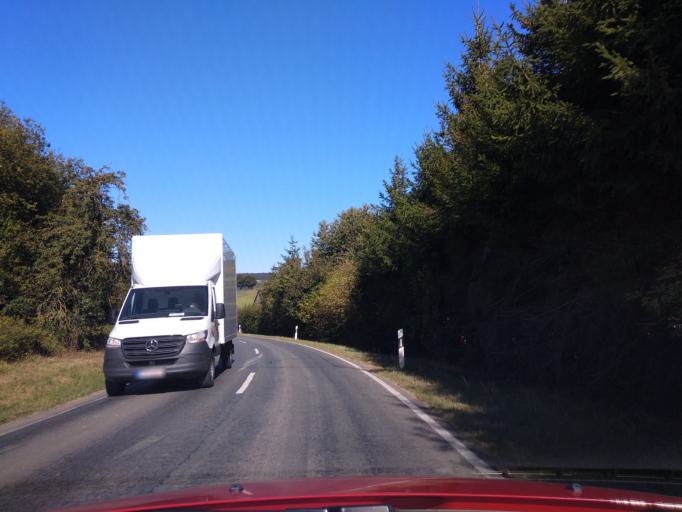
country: DE
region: North Rhine-Westphalia
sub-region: Regierungsbezirk Detmold
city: Hoexter
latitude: 51.7667
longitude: 9.2946
